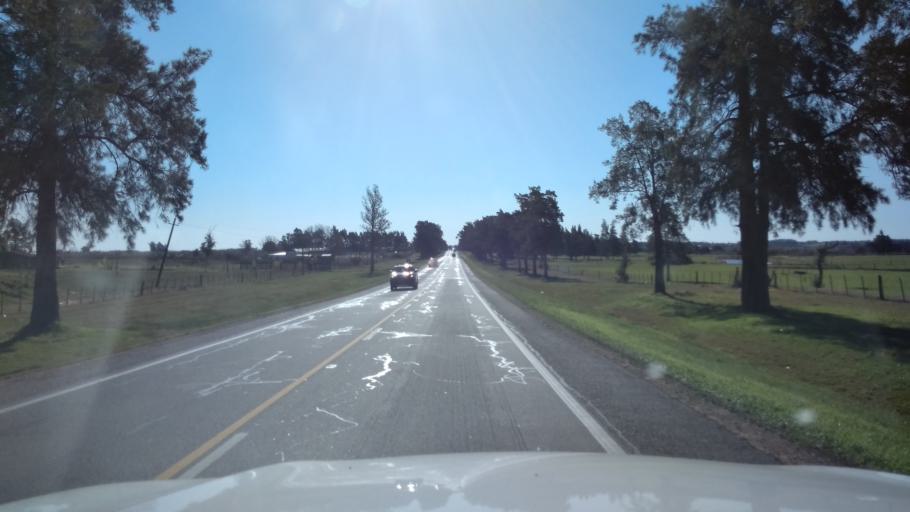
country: UY
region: Canelones
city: San Jacinto
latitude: -34.5824
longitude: -55.8427
